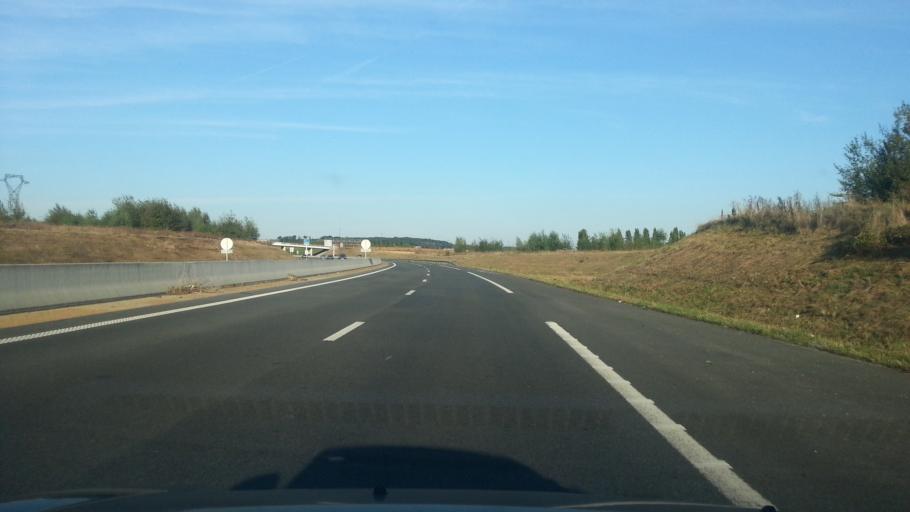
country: FR
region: Picardie
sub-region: Departement de l'Oise
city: Breuil-le-Sec
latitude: 49.3796
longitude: 2.4477
